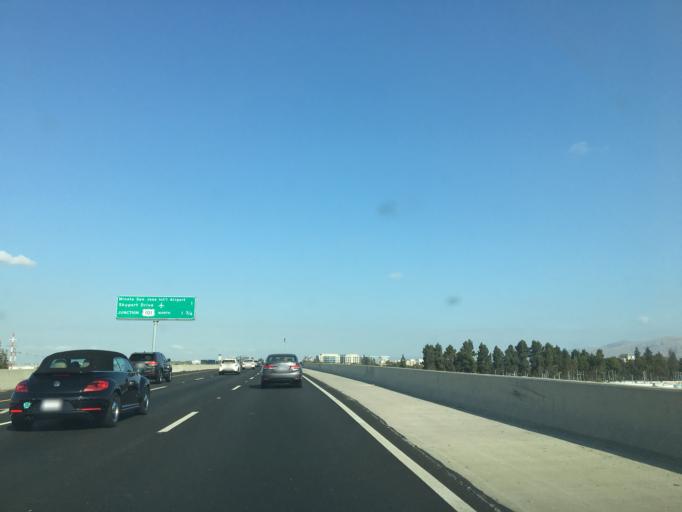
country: US
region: California
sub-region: Santa Clara County
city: San Jose
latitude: 37.3518
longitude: -121.9098
